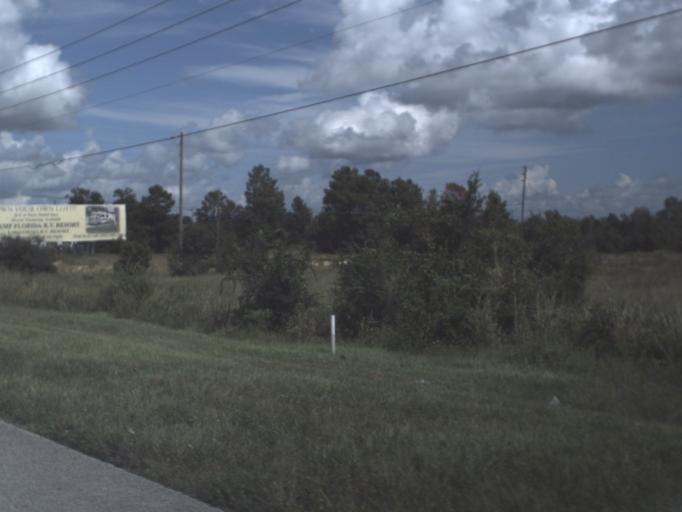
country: US
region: Florida
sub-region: Highlands County
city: Lake Placid
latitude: 27.2629
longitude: -81.3456
